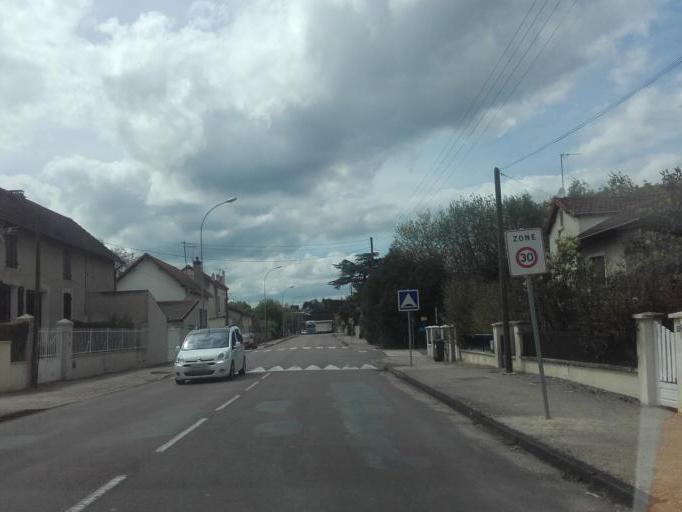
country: FR
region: Bourgogne
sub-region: Departement de Saone-et-Loire
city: Saint-Remy
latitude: 46.7740
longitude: 4.8233
